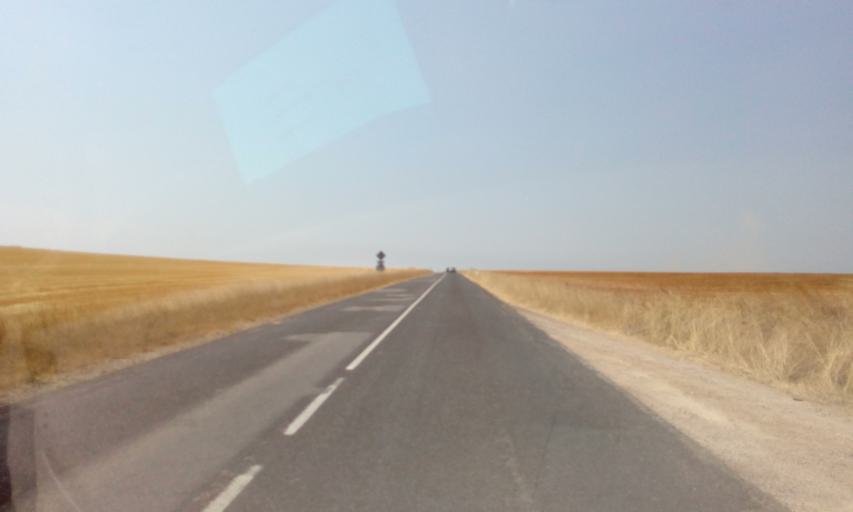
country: FR
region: Lorraine
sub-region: Departement de la Meuse
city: Montmedy
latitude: 49.4642
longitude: 5.3965
